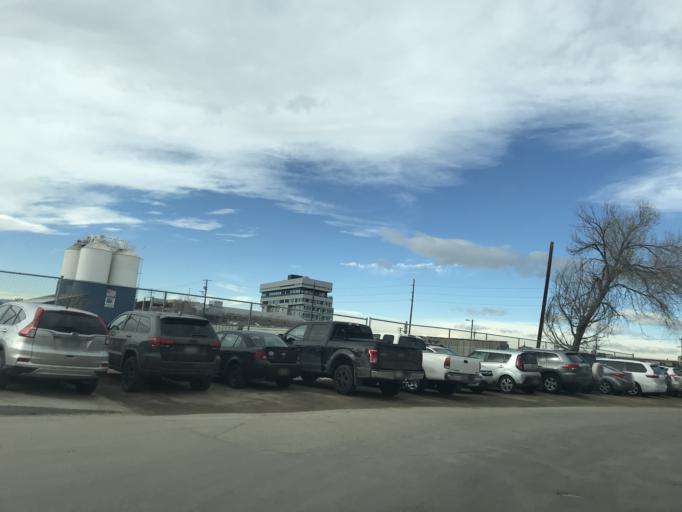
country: US
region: Colorado
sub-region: Denver County
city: Denver
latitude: 39.7691
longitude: -104.9770
